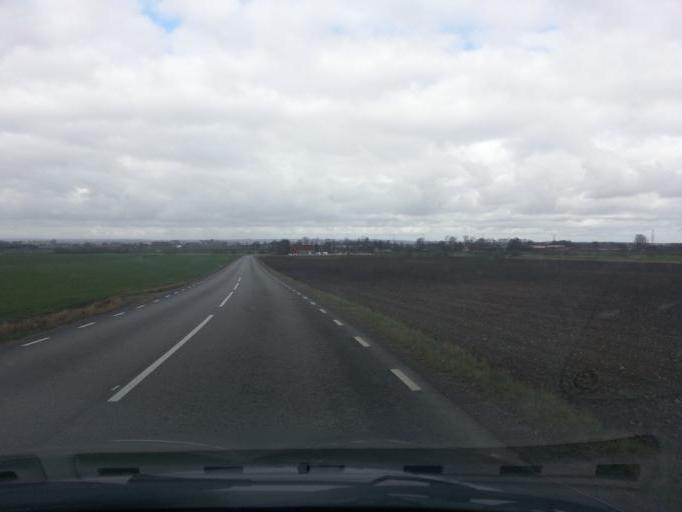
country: SE
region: Skane
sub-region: Astorps Kommun
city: Astorp
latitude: 56.1298
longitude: 13.0032
